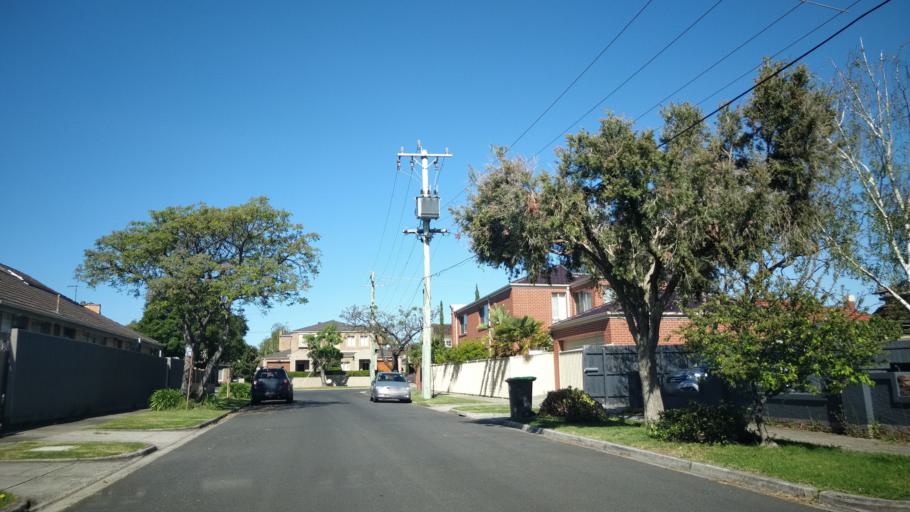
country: AU
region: Victoria
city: Ormond
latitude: -37.9045
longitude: 145.0273
